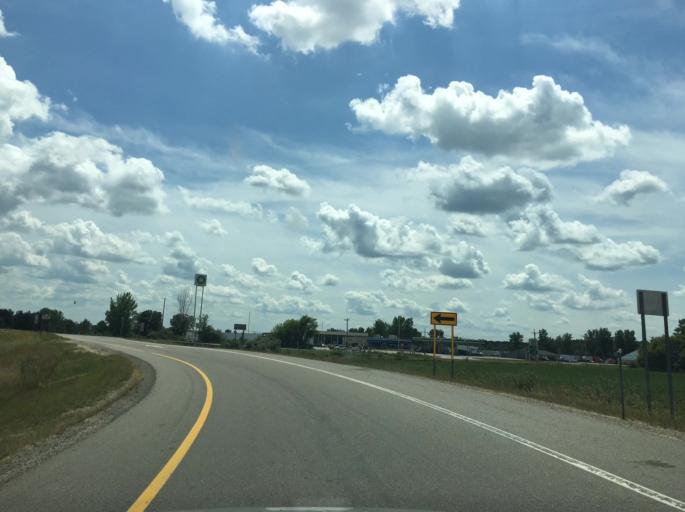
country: US
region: Michigan
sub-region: Bay County
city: Pinconning
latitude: 43.8553
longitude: -84.0230
